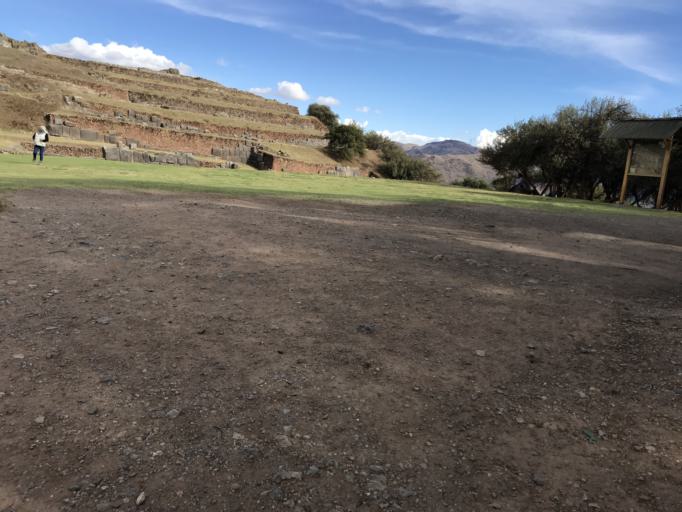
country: PE
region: Cusco
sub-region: Provincia de Cusco
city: Cusco
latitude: -13.5081
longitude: -71.9844
